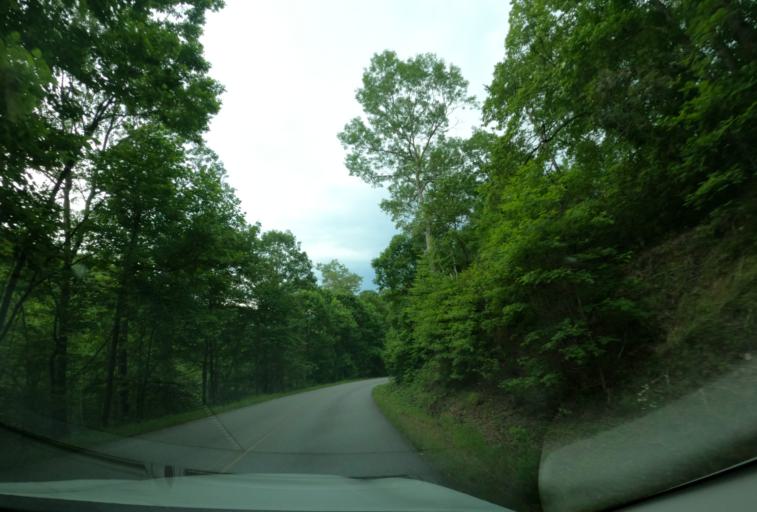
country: US
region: North Carolina
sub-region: Transylvania County
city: Brevard
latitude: 35.2819
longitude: -82.8151
